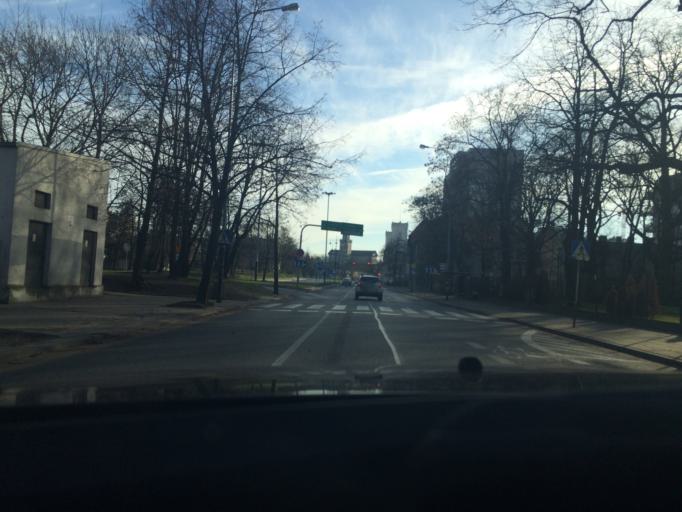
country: PL
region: Lodz Voivodeship
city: Lodz
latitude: 51.7619
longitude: 19.4409
